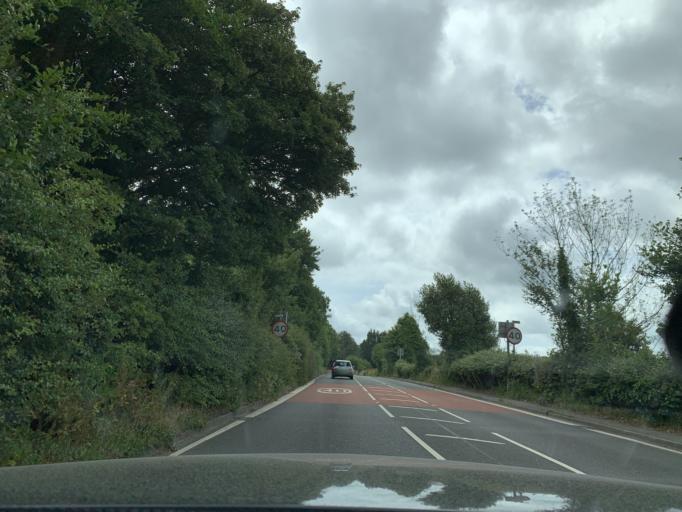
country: GB
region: England
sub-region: East Sussex
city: Robertsbridge
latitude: 51.0129
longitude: 0.4727
